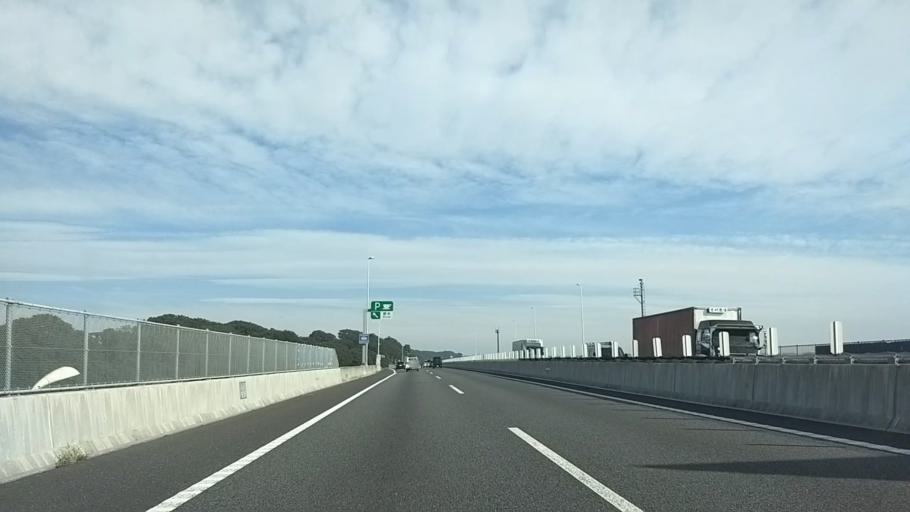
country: JP
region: Kanagawa
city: Zama
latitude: 35.4860
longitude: 139.3706
